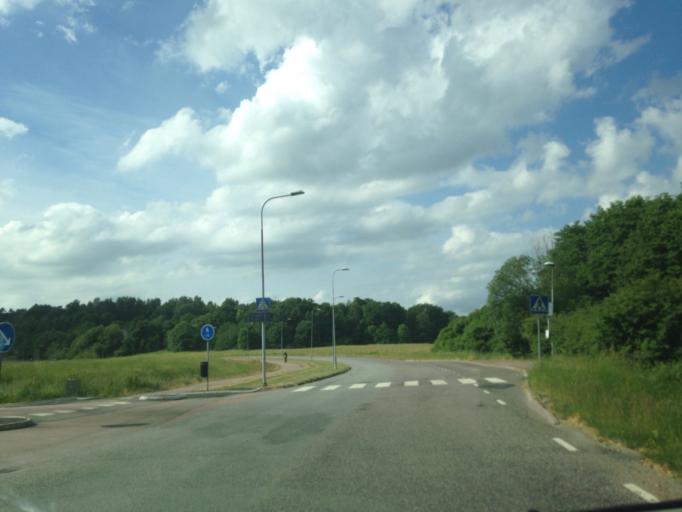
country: SE
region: Vaestra Goetaland
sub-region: Goteborg
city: Goeteborg
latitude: 57.7601
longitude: 11.9376
